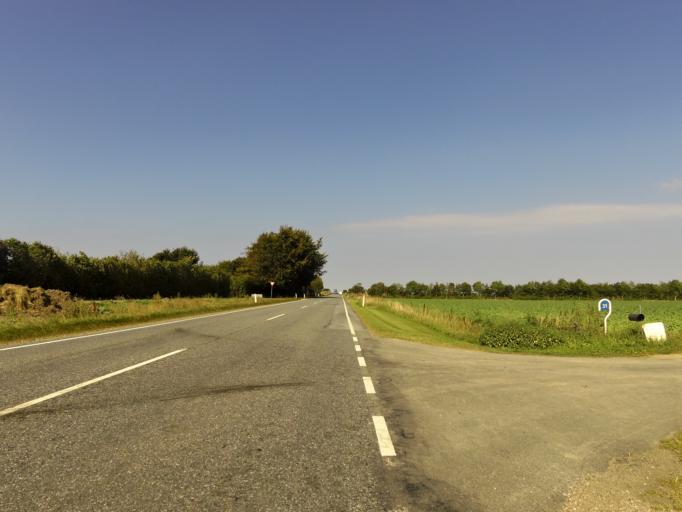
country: DK
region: South Denmark
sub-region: Vejen Kommune
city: Vejen
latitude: 55.3962
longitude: 9.1502
